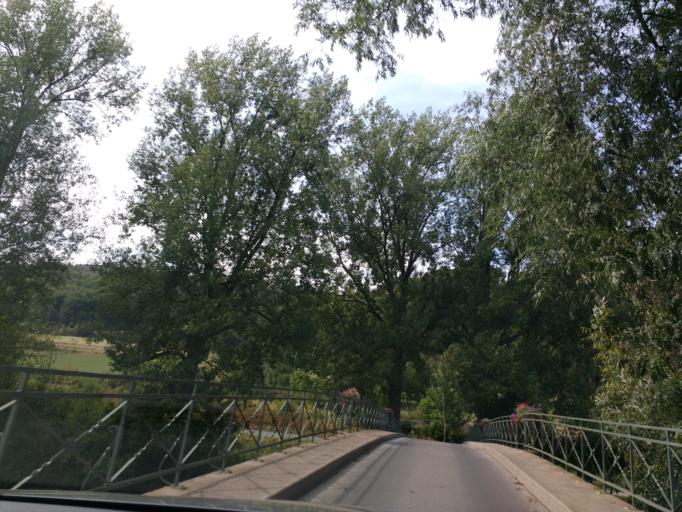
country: DE
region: Lower Saxony
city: Bad Pyrmont
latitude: 51.9882
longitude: 9.3110
